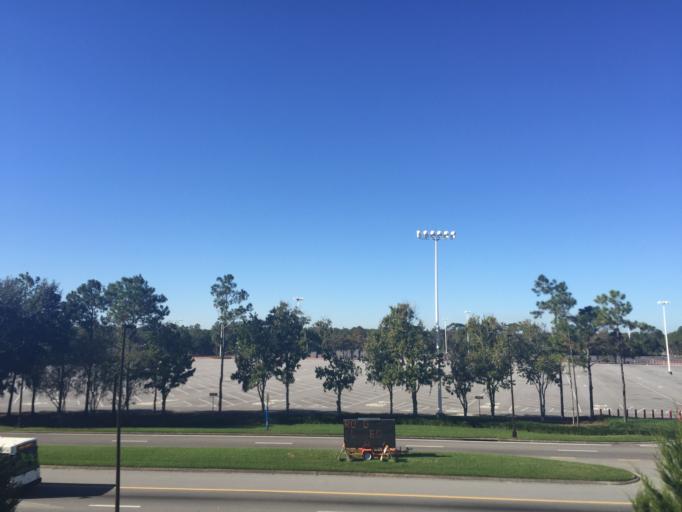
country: US
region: Florida
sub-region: Osceola County
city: Celebration
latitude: 28.4011
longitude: -81.5741
